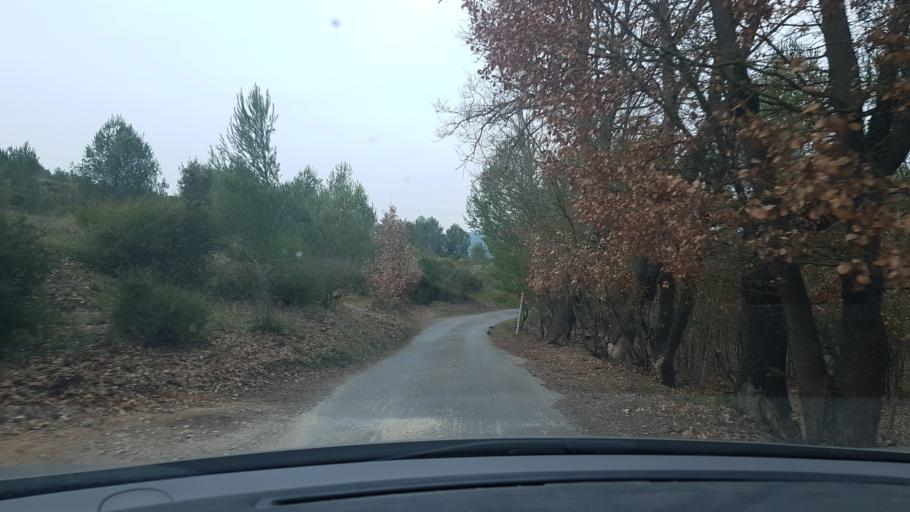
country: FR
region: Provence-Alpes-Cote d'Azur
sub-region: Departement des Bouches-du-Rhone
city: Gardanne
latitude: 43.4757
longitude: 5.4639
